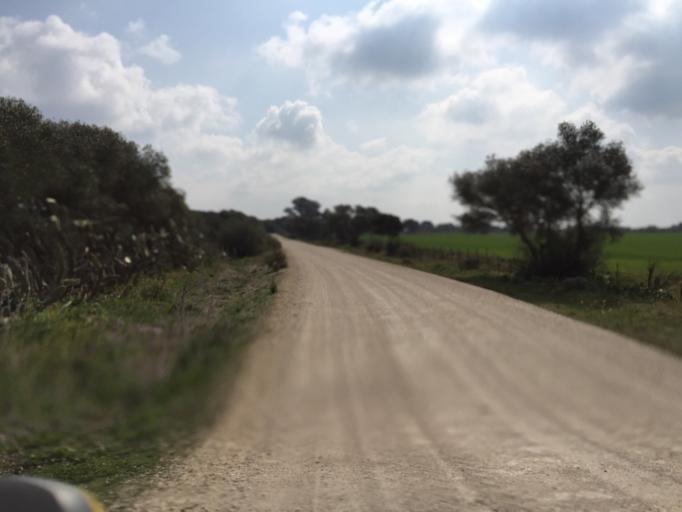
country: ES
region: Andalusia
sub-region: Provincia de Cadiz
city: Benalup-Casas Viejas
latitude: 36.3267
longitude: -5.8871
